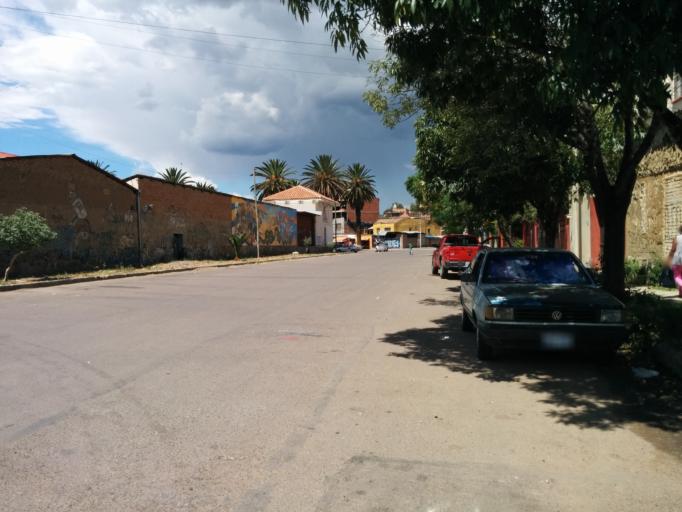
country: BO
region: Cochabamba
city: Cochabamba
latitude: -17.4004
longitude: -66.1663
